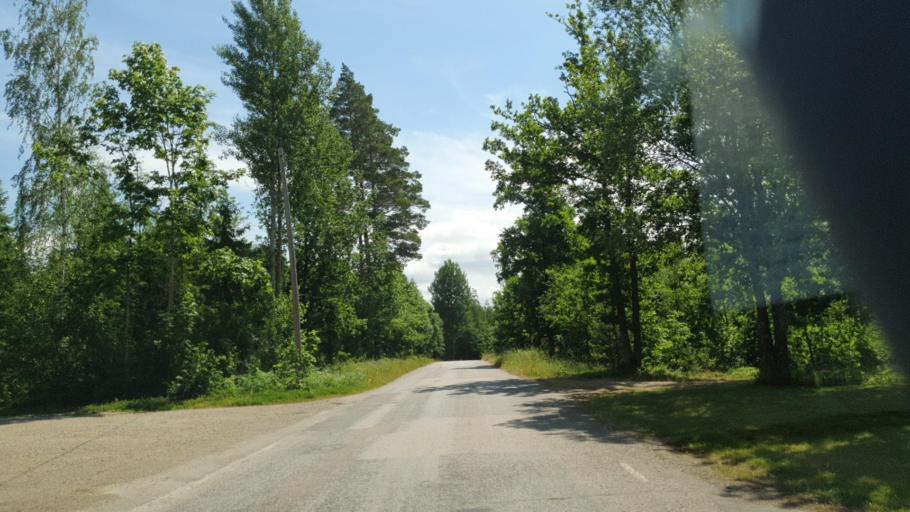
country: SE
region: Kronoberg
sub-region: Lessebo Kommun
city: Hovmantorp
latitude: 56.7438
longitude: 15.1791
